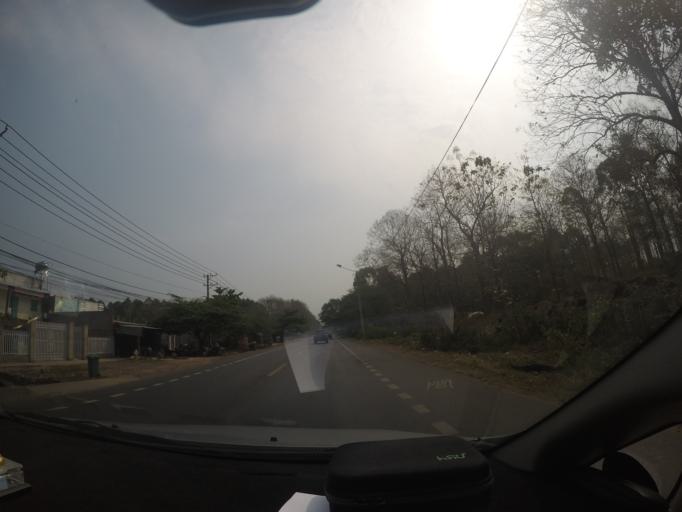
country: VN
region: Dong Nai
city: Tan Phu
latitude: 11.2398
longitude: 107.3919
